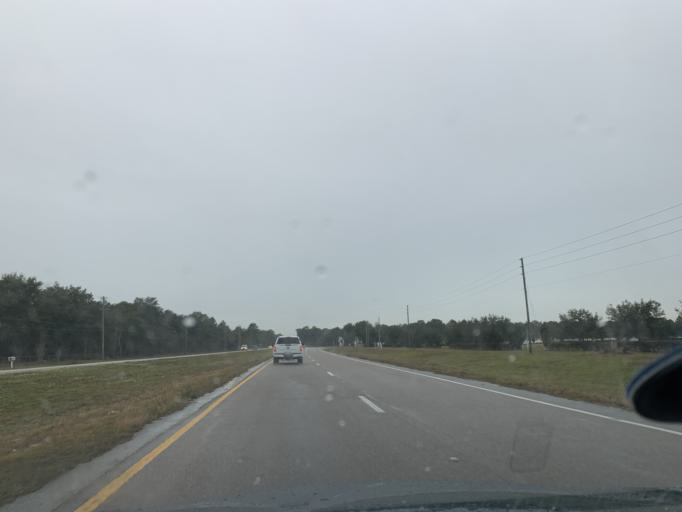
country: US
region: Florida
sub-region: Hernando County
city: Masaryktown
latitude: 28.4340
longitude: -82.4928
